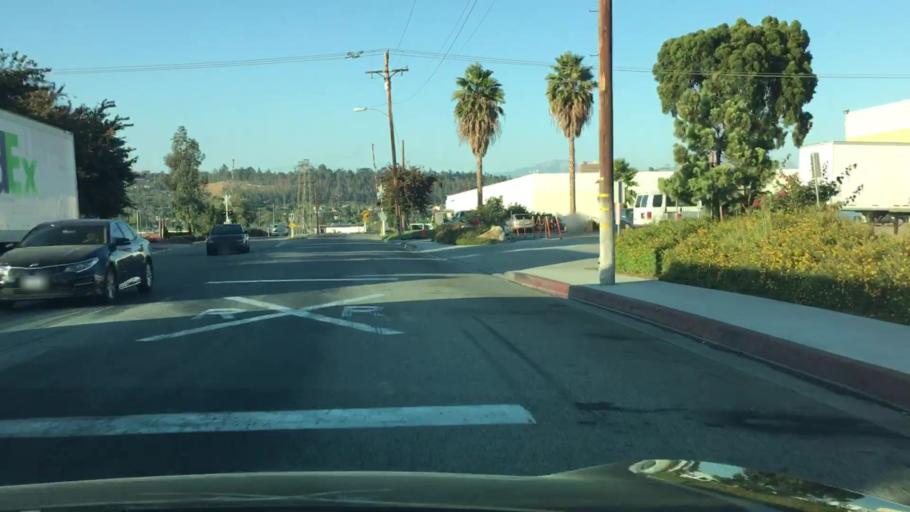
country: US
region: California
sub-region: Los Angeles County
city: La Puente
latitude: 34.0063
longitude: -117.9434
